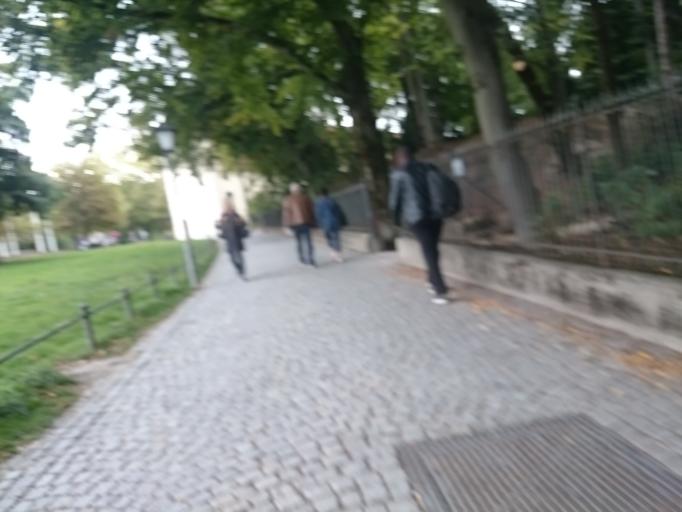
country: DE
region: Bavaria
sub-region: Upper Bavaria
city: Munich
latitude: 48.1438
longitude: 11.5826
